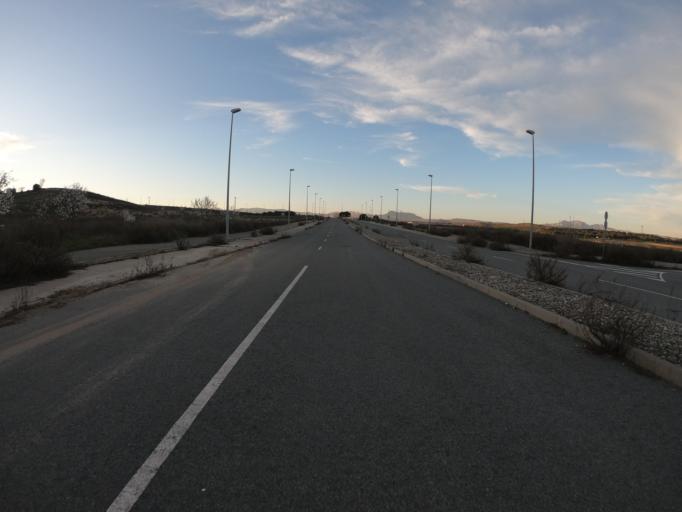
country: ES
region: Basque Country
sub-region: Provincia de Alava
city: Oyon
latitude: 42.4843
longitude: -2.4149
